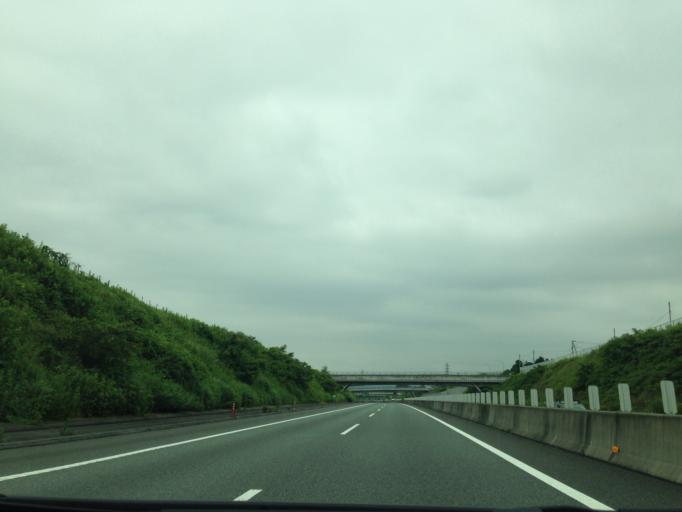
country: JP
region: Shizuoka
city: Fuji
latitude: 35.1999
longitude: 138.6886
